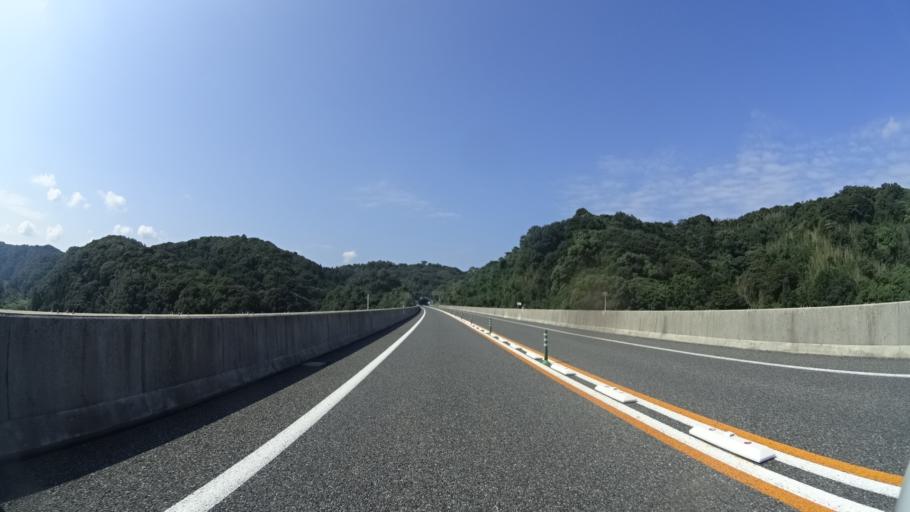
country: JP
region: Shimane
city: Gotsucho
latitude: 34.9680
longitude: 132.1704
